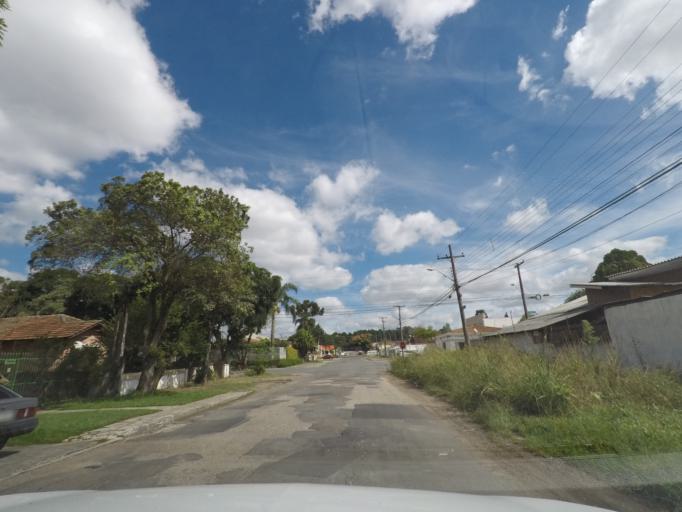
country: BR
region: Parana
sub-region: Sao Jose Dos Pinhais
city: Sao Jose dos Pinhais
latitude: -25.5071
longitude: -49.2304
